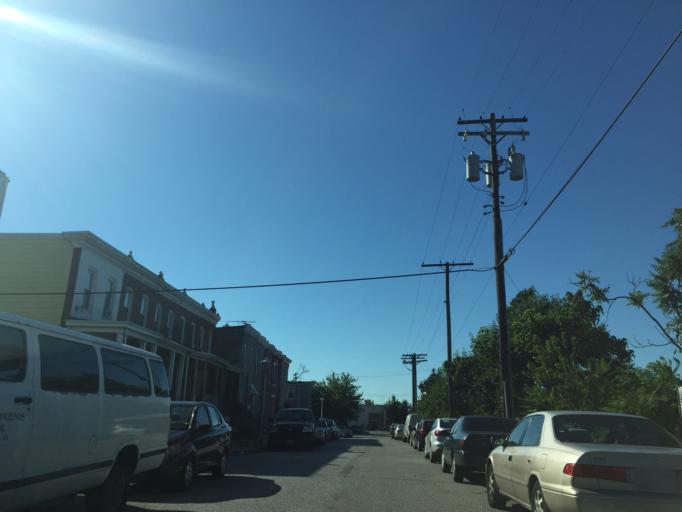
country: US
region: Maryland
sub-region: City of Baltimore
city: Baltimore
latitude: 39.3197
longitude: -76.6245
